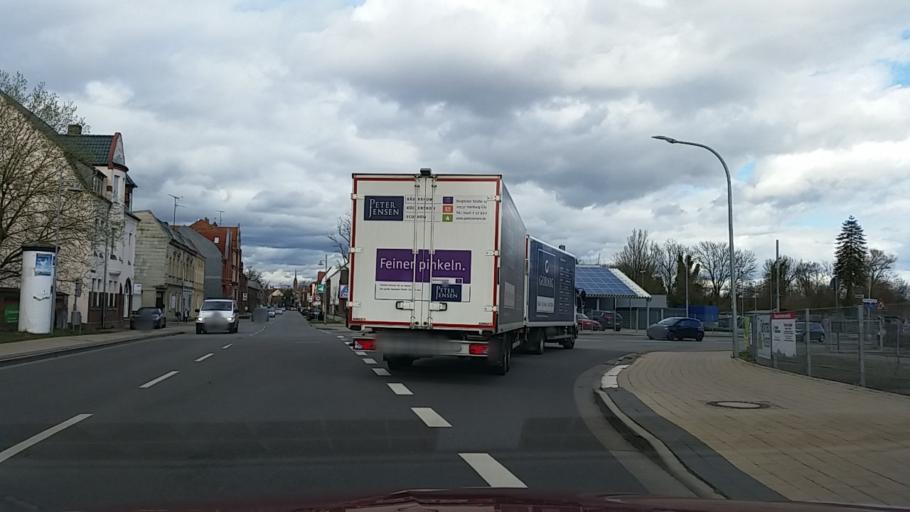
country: DE
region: Saxony-Anhalt
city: Salzwedel
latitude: 52.8438
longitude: 11.1520
